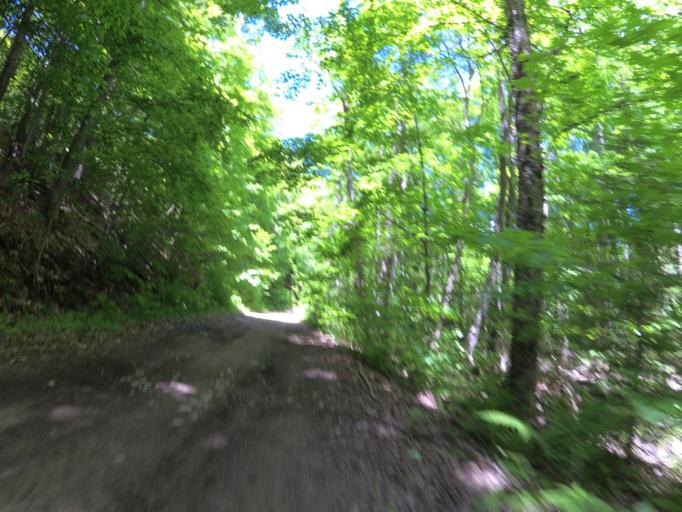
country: CA
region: Ontario
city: Renfrew
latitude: 45.0376
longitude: -76.8717
